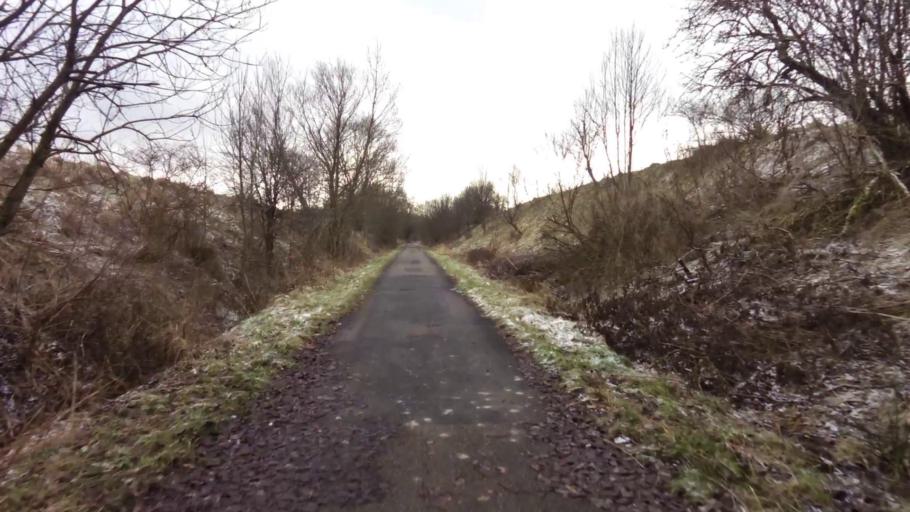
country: PL
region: West Pomeranian Voivodeship
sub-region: Powiat drawski
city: Zlocieniec
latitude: 53.5993
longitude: 16.0465
